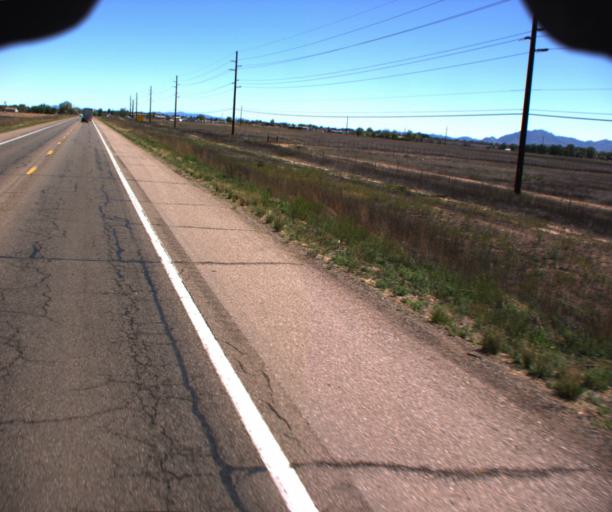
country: US
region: Arizona
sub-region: Yavapai County
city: Chino Valley
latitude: 34.8103
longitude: -112.4519
